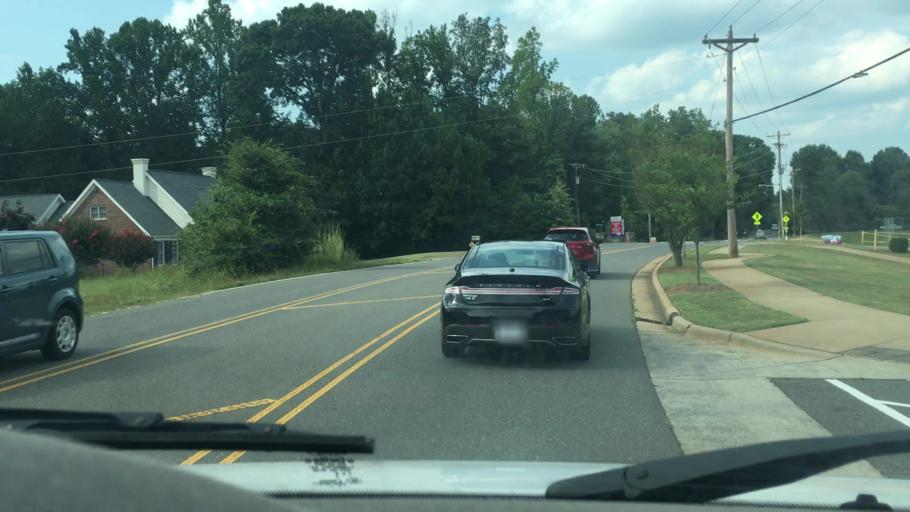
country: US
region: North Carolina
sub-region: Mecklenburg County
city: Huntersville
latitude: 35.4129
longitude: -80.8734
